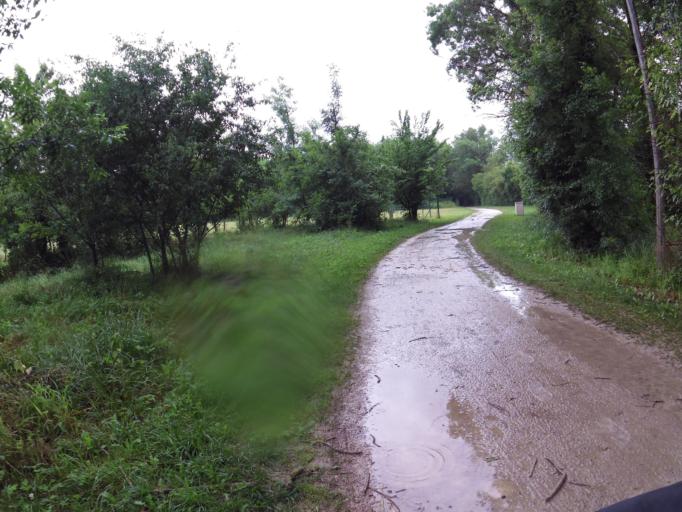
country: FR
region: Poitou-Charentes
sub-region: Departement de la Charente
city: Gond-Pontouvre
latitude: 45.6728
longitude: 0.1536
